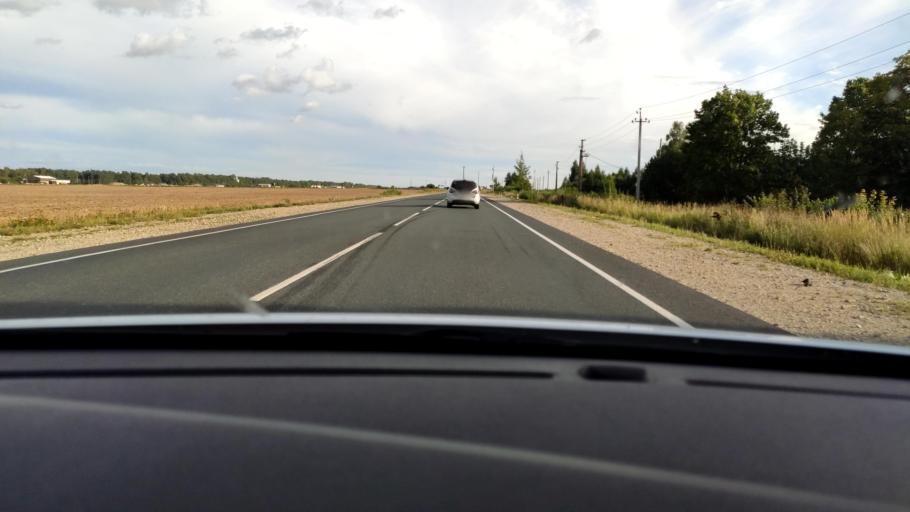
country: RU
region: Mariy-El
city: Suslonger
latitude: 56.2209
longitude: 48.2360
